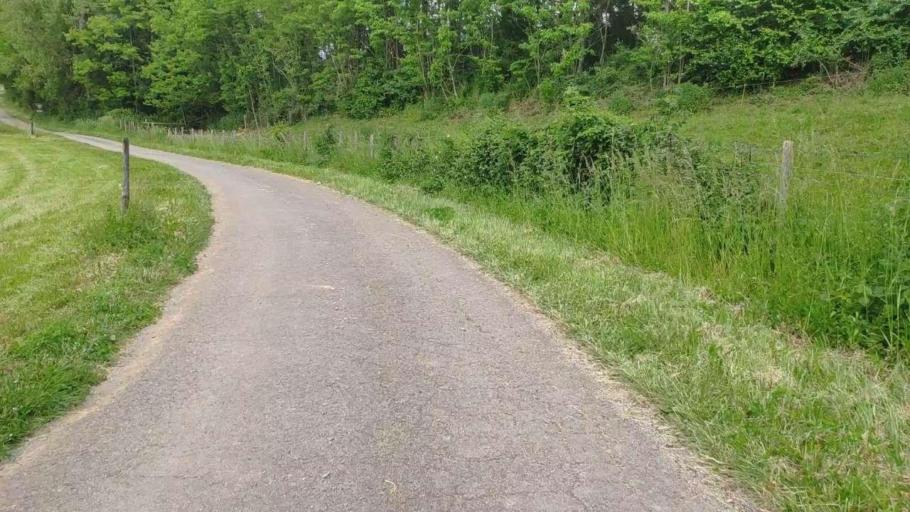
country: FR
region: Franche-Comte
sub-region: Departement du Jura
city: Bletterans
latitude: 46.7336
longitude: 5.4979
